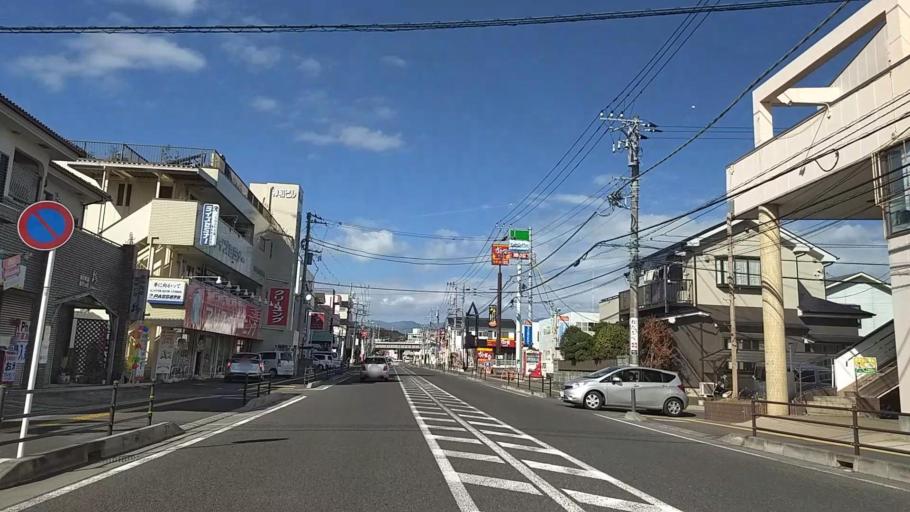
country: JP
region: Kanagawa
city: Ninomiya
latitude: 35.3064
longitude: 139.2541
